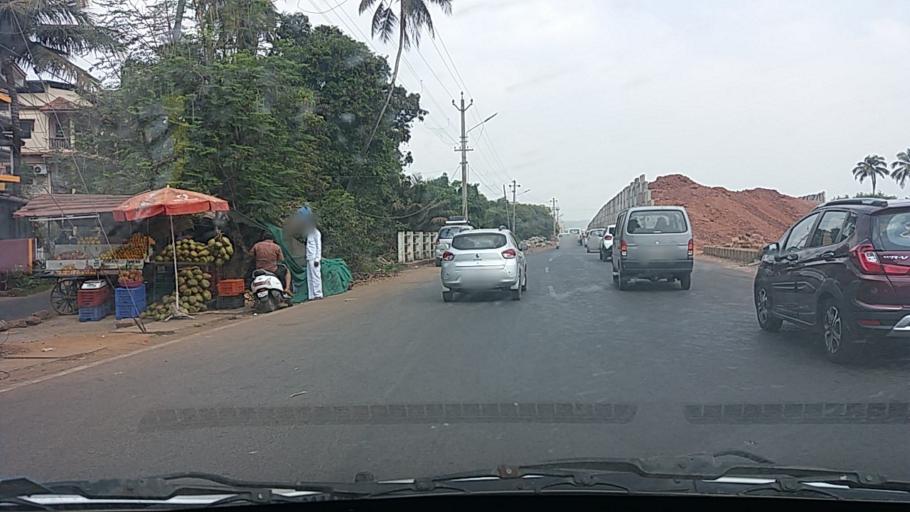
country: IN
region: Goa
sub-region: North Goa
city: Bambolim
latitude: 15.4787
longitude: 73.8484
